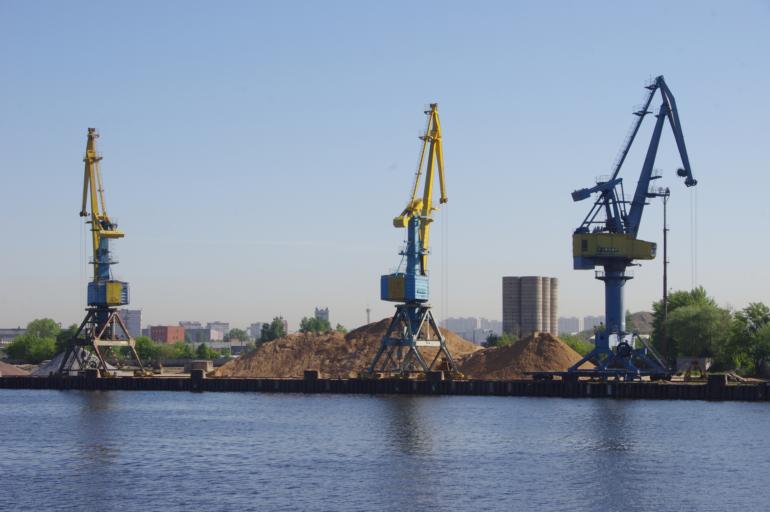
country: RU
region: Moscow
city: Kolomenskoye
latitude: 55.6914
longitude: 37.7084
